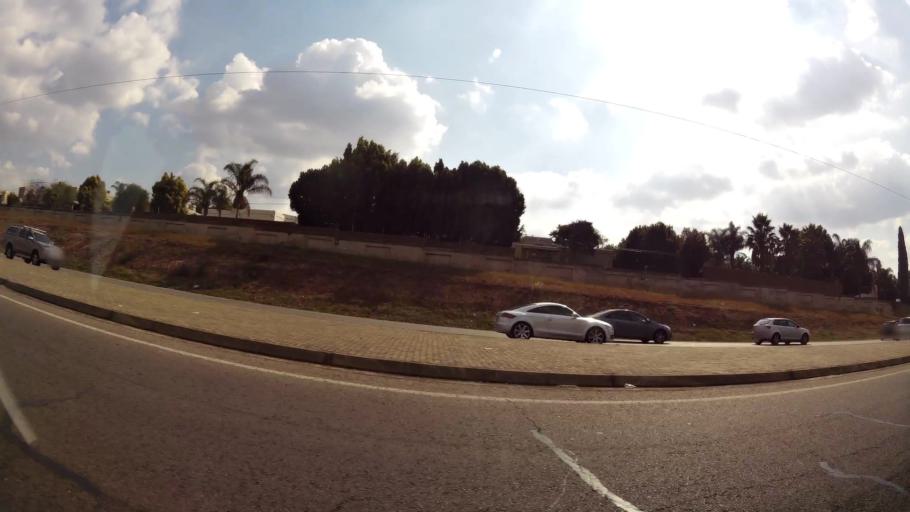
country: ZA
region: Gauteng
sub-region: City of Tshwane Metropolitan Municipality
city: Centurion
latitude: -25.8176
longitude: 28.2743
